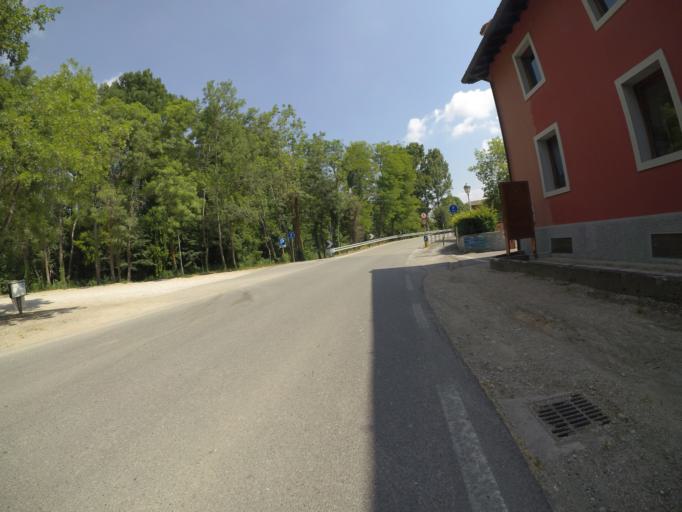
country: IT
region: Friuli Venezia Giulia
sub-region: Provincia di Udine
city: Teor
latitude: 45.8717
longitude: 13.0831
